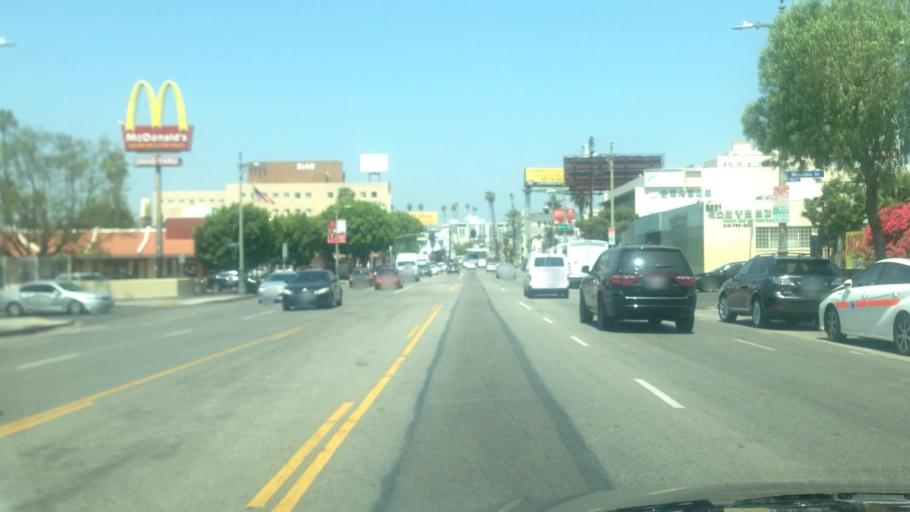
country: US
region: California
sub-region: Los Angeles County
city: Echo Park
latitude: 34.0510
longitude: -118.2783
